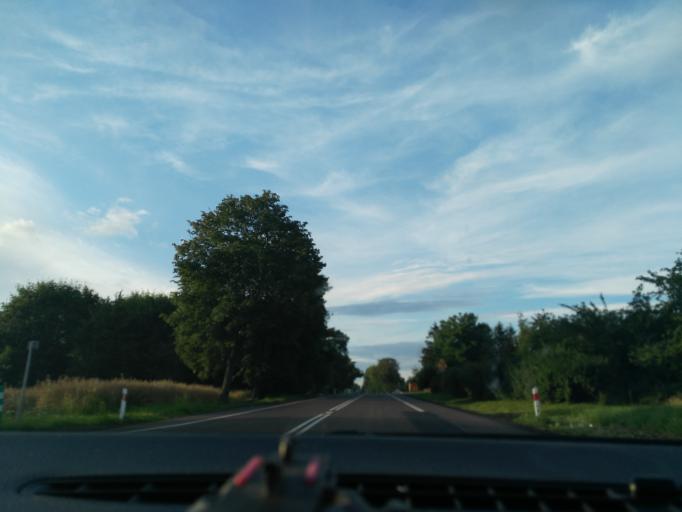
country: PL
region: Lublin Voivodeship
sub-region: Powiat krasnicki
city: Wilkolaz
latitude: 51.0560
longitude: 22.3832
